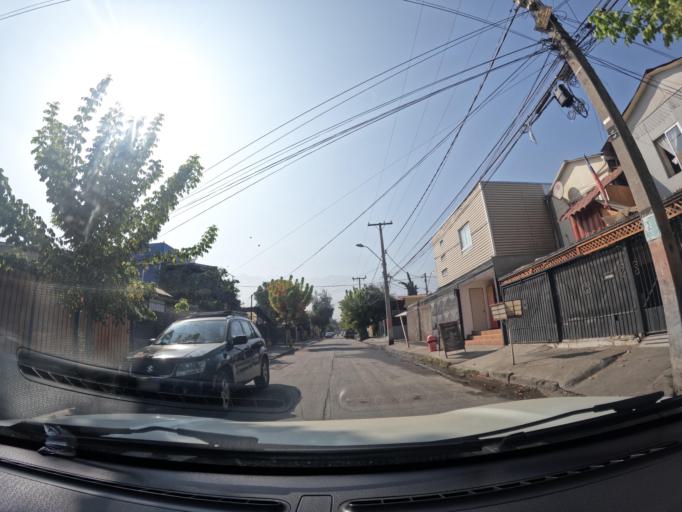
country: CL
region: Santiago Metropolitan
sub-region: Provincia de Santiago
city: Villa Presidente Frei, Nunoa, Santiago, Chile
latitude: -33.4798
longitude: -70.5645
